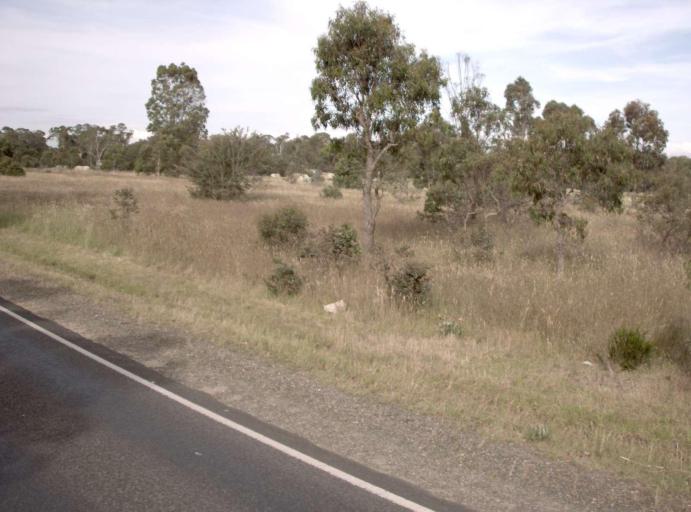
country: AU
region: Victoria
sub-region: Latrobe
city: Traralgon
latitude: -38.0668
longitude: 146.6175
